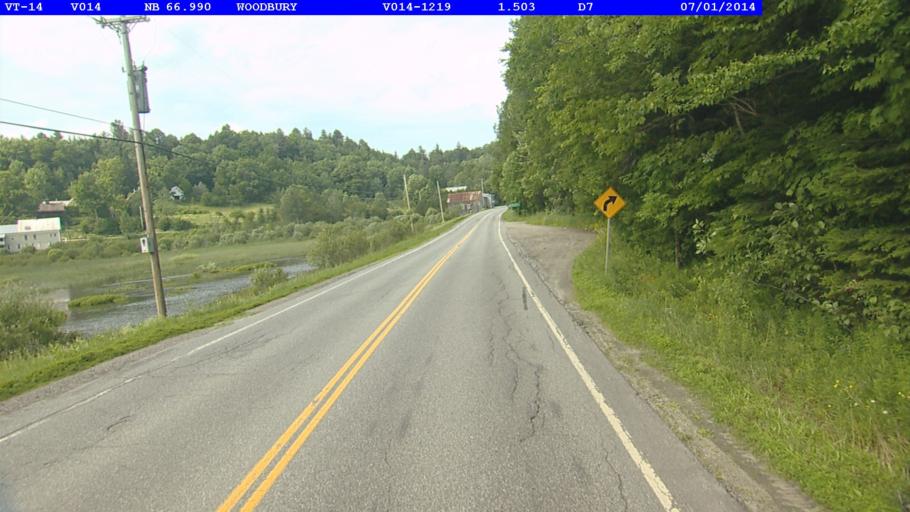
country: US
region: Vermont
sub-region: Caledonia County
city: Hardwick
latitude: 44.4129
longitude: -72.4192
